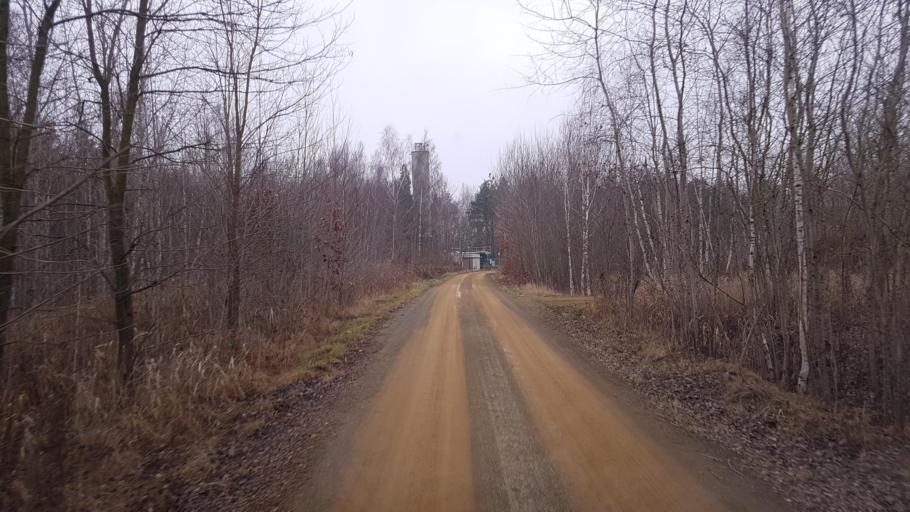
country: DE
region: Brandenburg
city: Plessa
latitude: 51.4962
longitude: 13.6593
